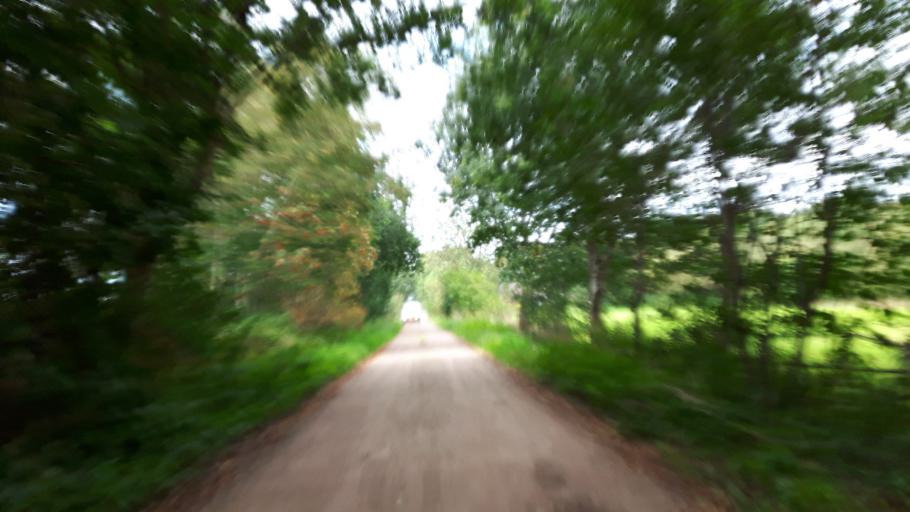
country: NL
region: Groningen
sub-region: Gemeente Leek
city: Leek
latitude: 53.0813
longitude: 6.3340
